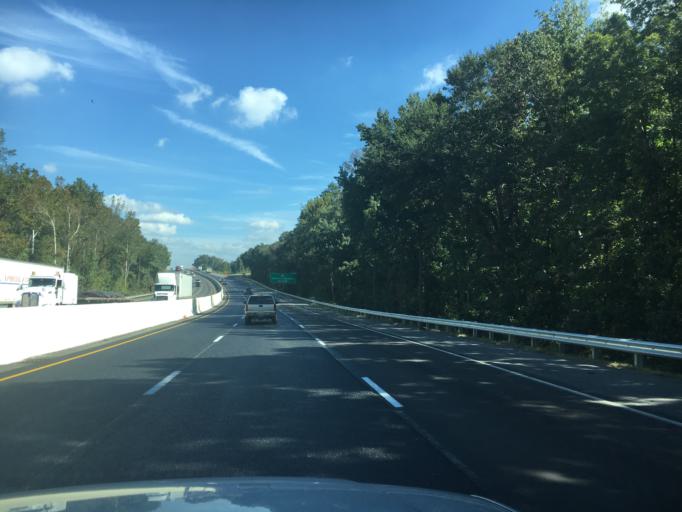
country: US
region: South Carolina
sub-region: Spartanburg County
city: Wellford
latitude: 34.9340
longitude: -82.0788
